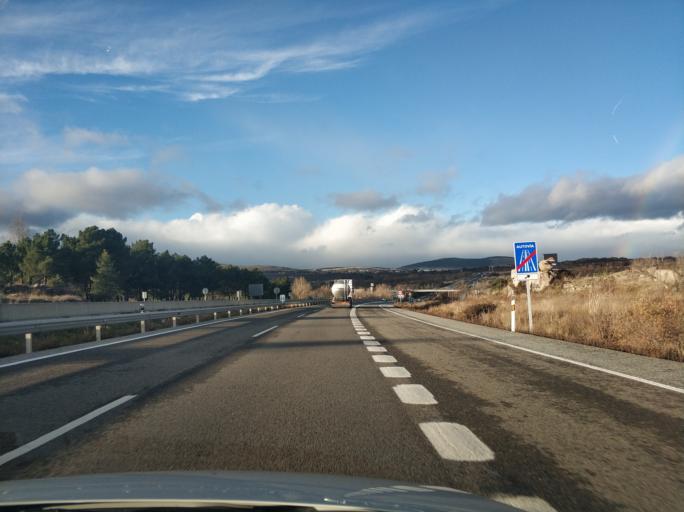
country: ES
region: Madrid
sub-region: Provincia de Madrid
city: La Cabrera
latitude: 40.9012
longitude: -3.6076
